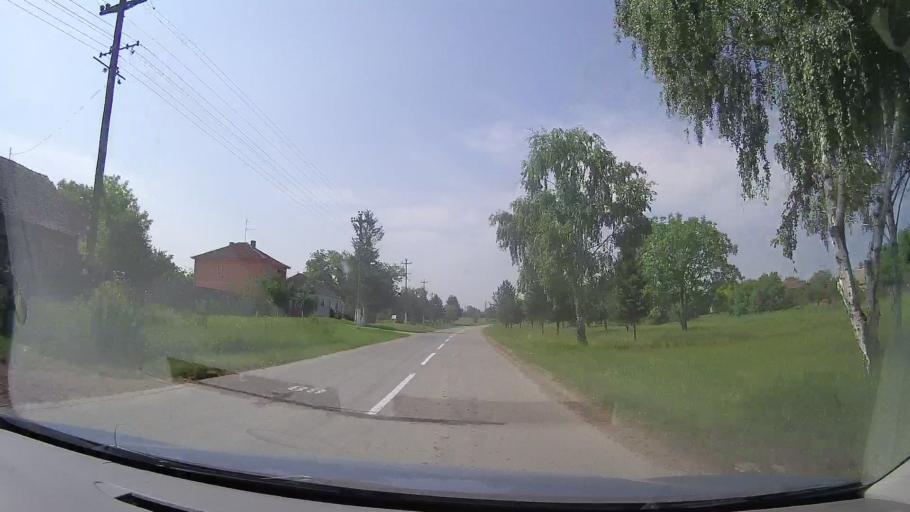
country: RS
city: Samos
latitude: 45.1990
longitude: 20.7717
